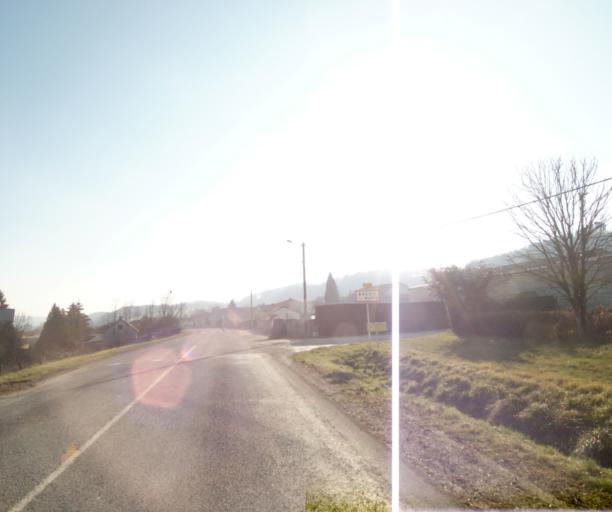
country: FR
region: Champagne-Ardenne
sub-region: Departement de la Haute-Marne
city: Chevillon
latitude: 48.5081
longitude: 5.1131
